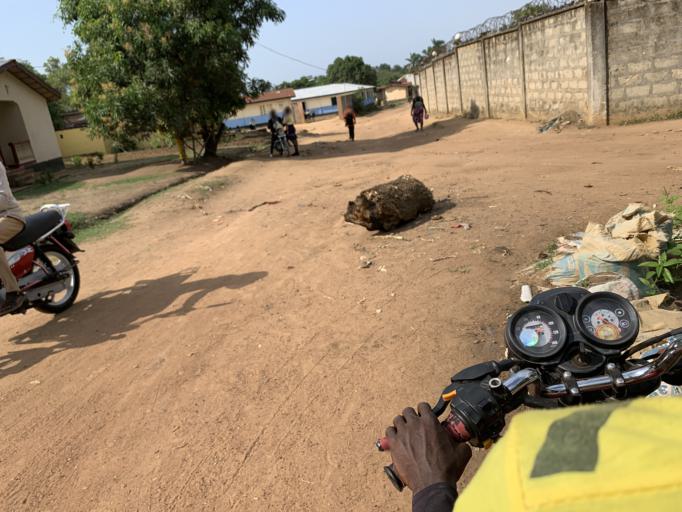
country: SL
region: Western Area
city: Waterloo
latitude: 8.3389
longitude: -13.0431
